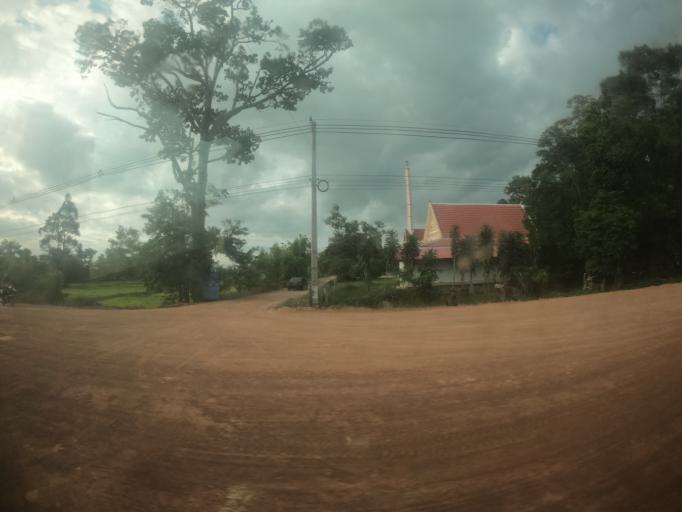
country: TH
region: Surin
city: Kap Choeng
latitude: 14.4671
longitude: 103.6318
